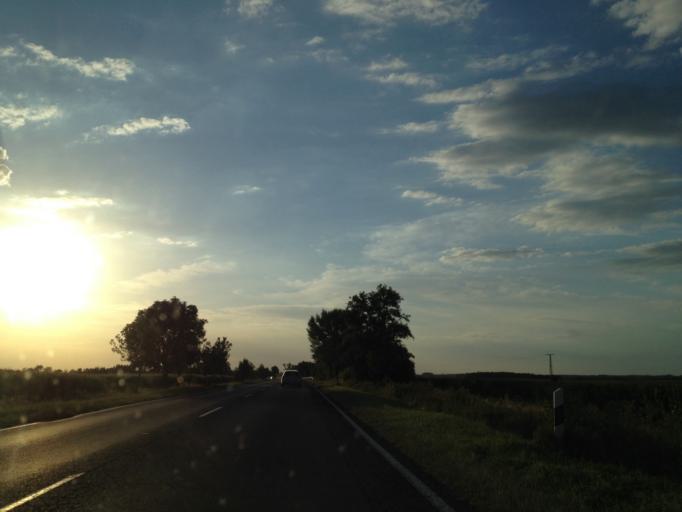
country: HU
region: Gyor-Moson-Sopron
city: Kimle
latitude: 47.7958
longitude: 17.3933
